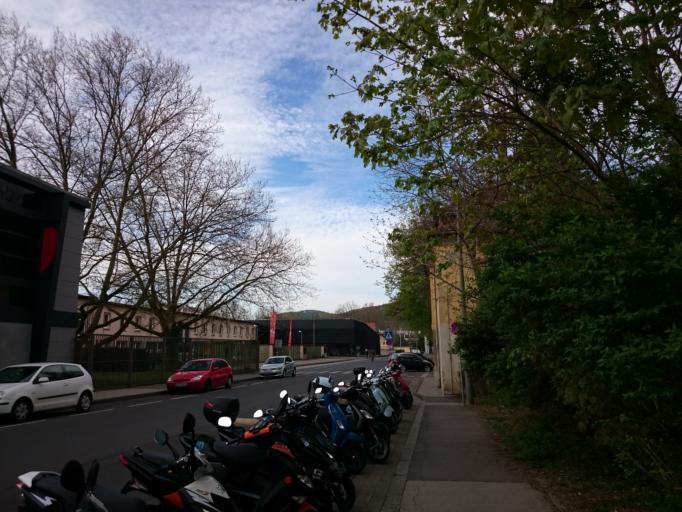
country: AT
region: Styria
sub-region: Graz Stadt
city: Wetzelsdorf
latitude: 47.0745
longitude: 15.3970
